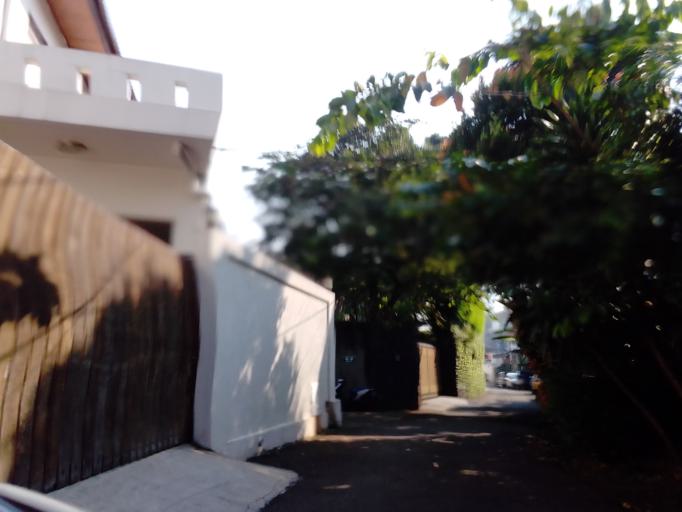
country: ID
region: Jakarta Raya
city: Jakarta
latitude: -6.2618
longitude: 106.8070
